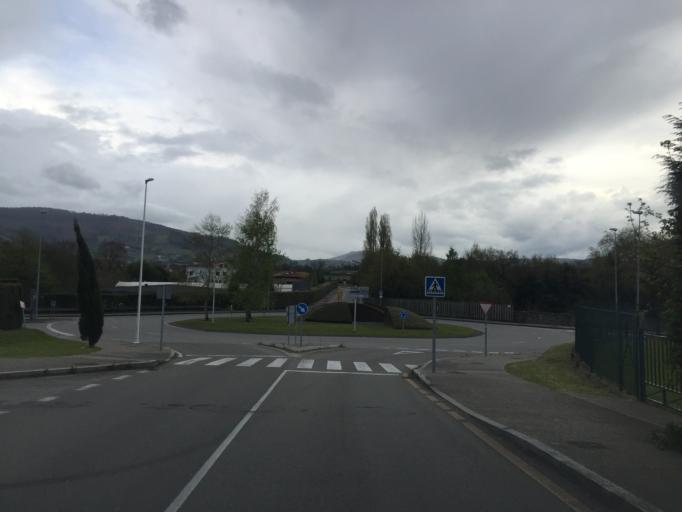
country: ES
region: Asturias
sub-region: Province of Asturias
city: Gijon
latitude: 43.5222
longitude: -5.6138
